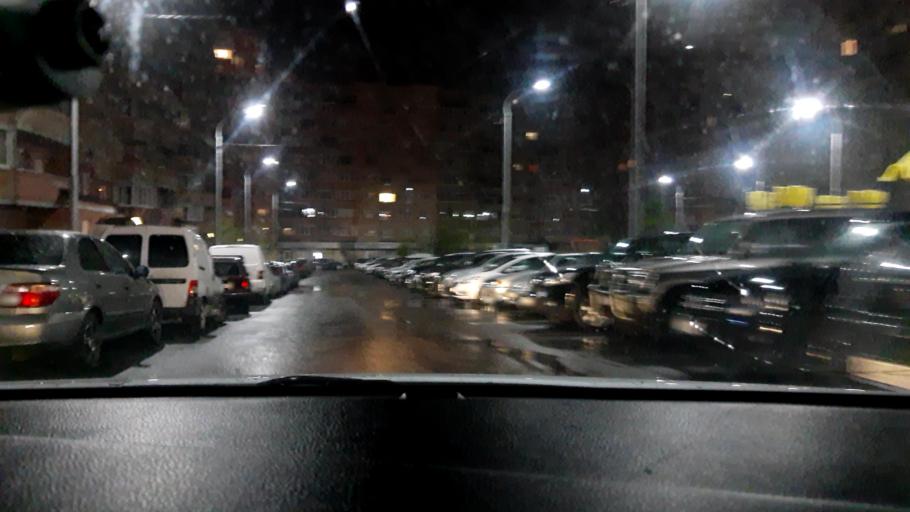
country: RU
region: Moskovskaya
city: Nakhabino
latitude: 55.8493
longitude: 37.1793
